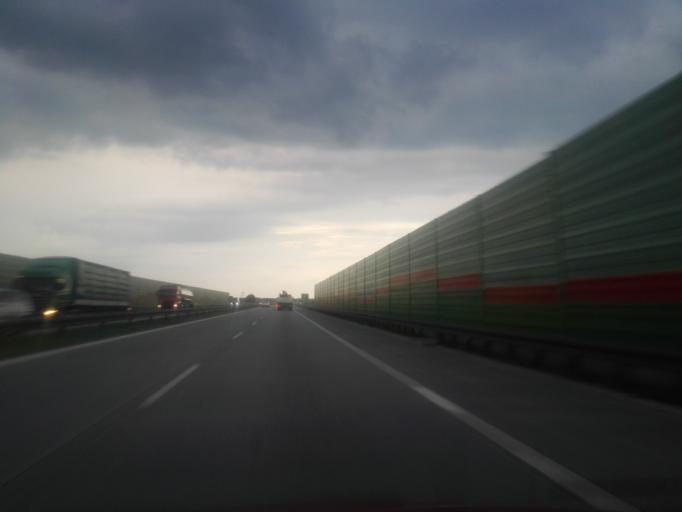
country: PL
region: Lodz Voivodeship
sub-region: Piotrkow Trybunalski
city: Piotrkow Trybunalski
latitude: 51.4431
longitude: 19.6983
